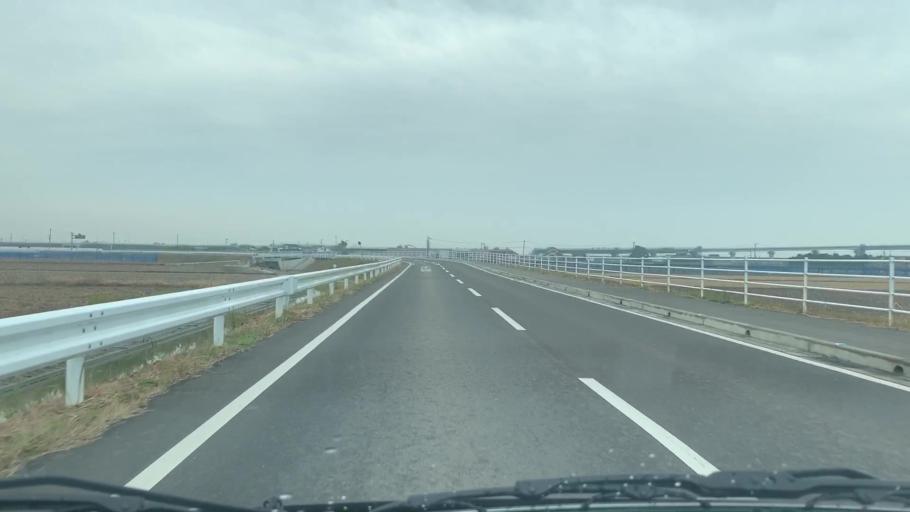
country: JP
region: Saga Prefecture
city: Saga-shi
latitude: 33.2033
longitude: 130.2071
